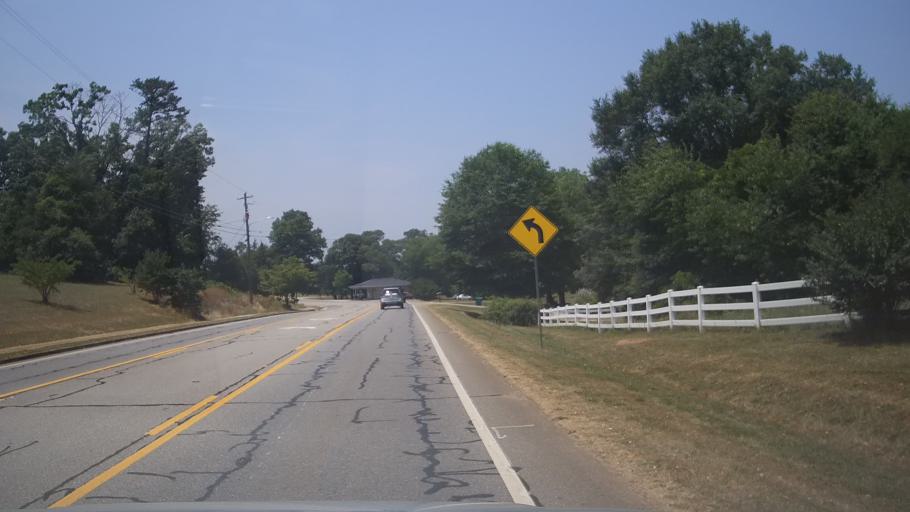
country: US
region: Georgia
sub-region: Hart County
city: Royston
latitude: 34.2854
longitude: -83.1422
